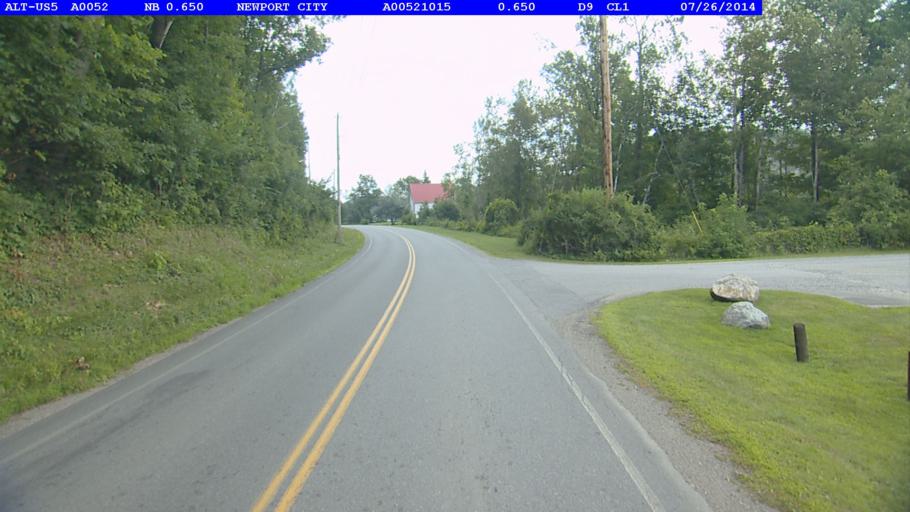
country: US
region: Vermont
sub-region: Orleans County
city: Newport
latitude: 44.9295
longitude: -72.2136
